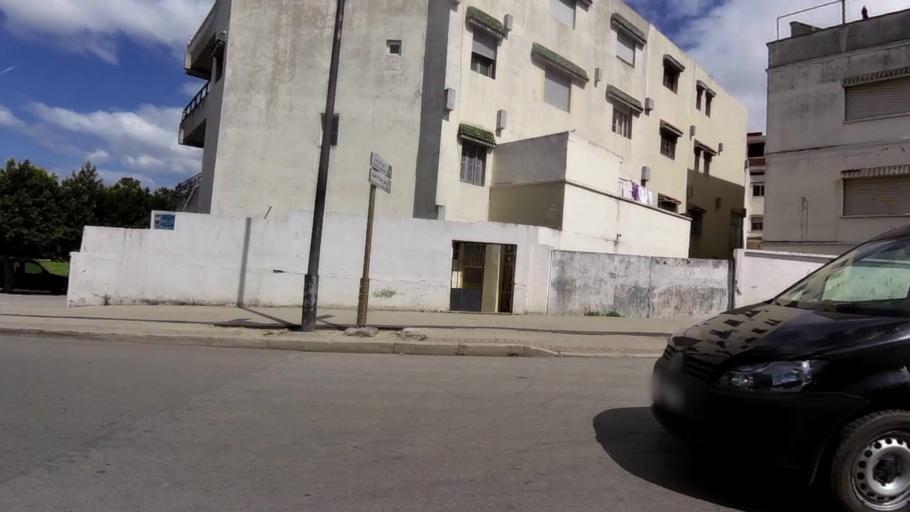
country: MA
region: Tanger-Tetouan
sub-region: Tanger-Assilah
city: Tangier
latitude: 35.7635
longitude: -5.8129
